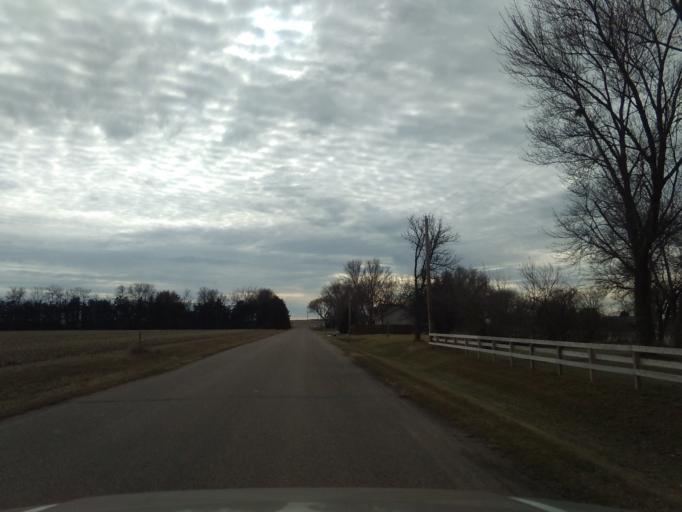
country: US
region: Nebraska
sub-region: Hall County
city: Grand Island
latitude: 40.7743
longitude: -98.4119
